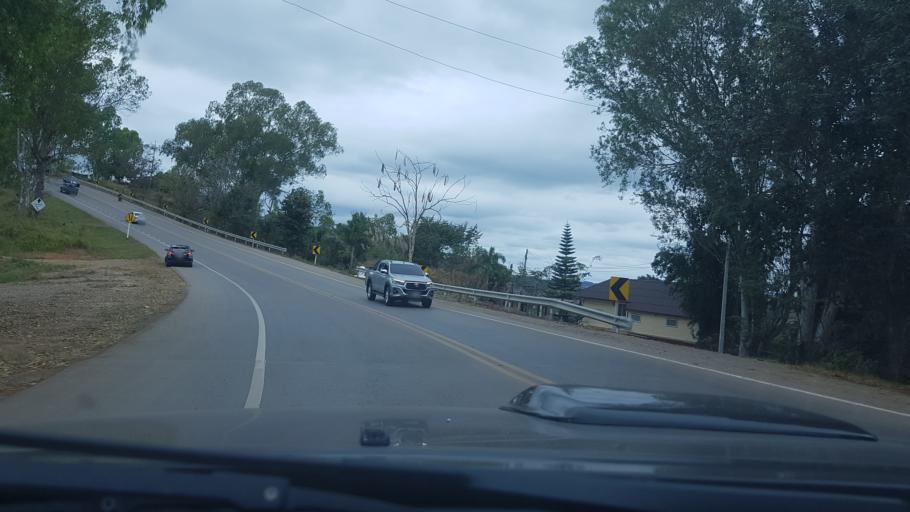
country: TH
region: Phetchabun
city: Khao Kho
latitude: 16.5630
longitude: 101.0104
